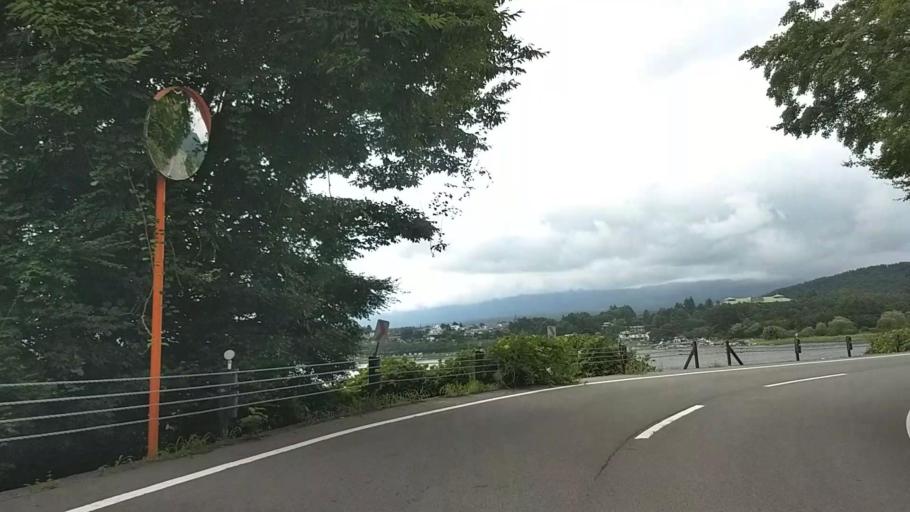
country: JP
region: Yamanashi
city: Fujikawaguchiko
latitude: 35.5149
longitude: 138.7407
